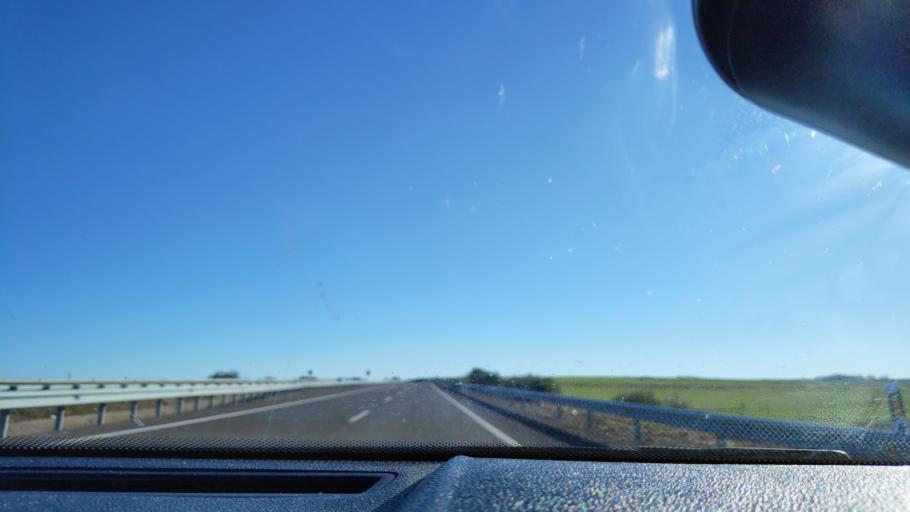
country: ES
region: Extremadura
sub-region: Provincia de Badajoz
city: Fuente de Cantos
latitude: 38.2065
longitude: -6.2864
